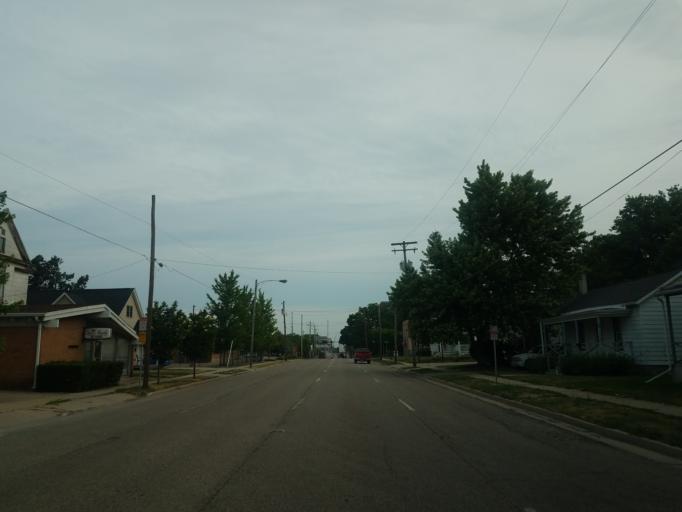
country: US
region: Illinois
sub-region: McLean County
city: Bloomington
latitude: 40.4696
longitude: -88.9932
